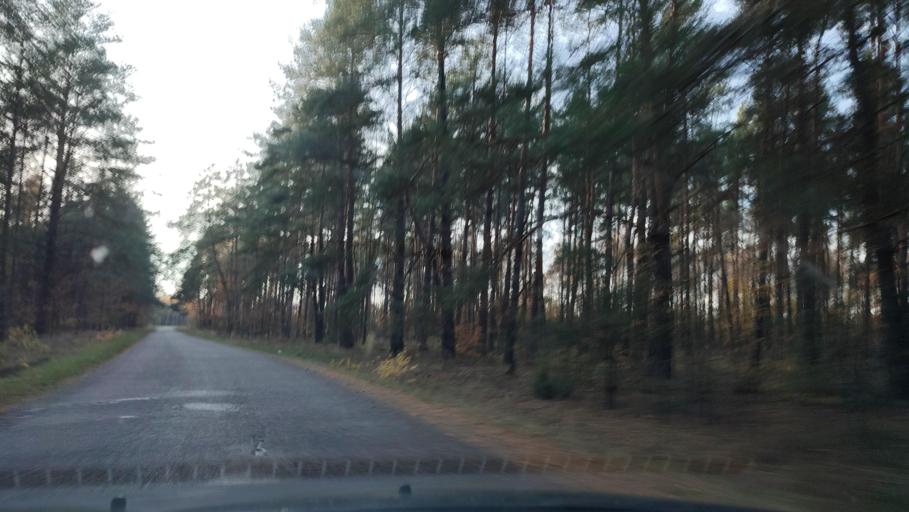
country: PL
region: Masovian Voivodeship
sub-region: Powiat przasnyski
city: Chorzele
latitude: 53.3312
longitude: 20.7301
